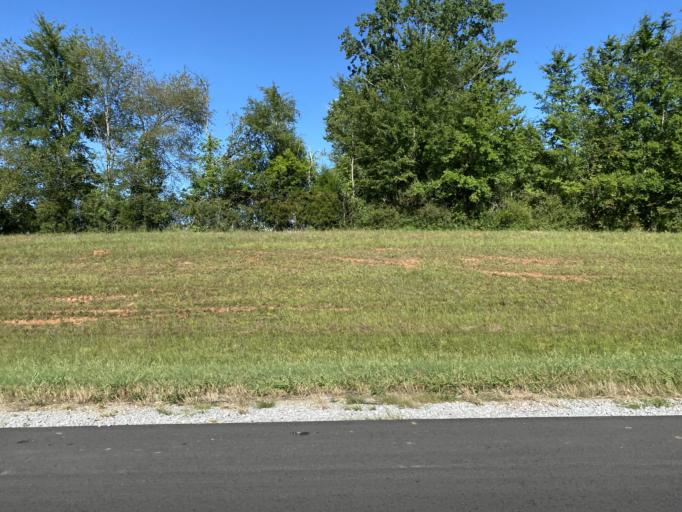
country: US
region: Alabama
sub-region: Limestone County
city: Athens
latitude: 34.7524
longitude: -86.9381
